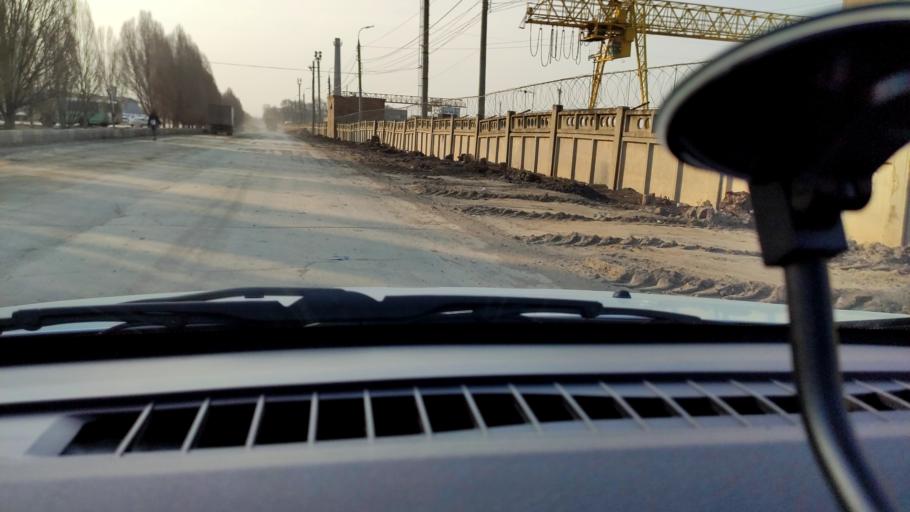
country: RU
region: Samara
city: Samara
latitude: 53.1850
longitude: 50.2601
